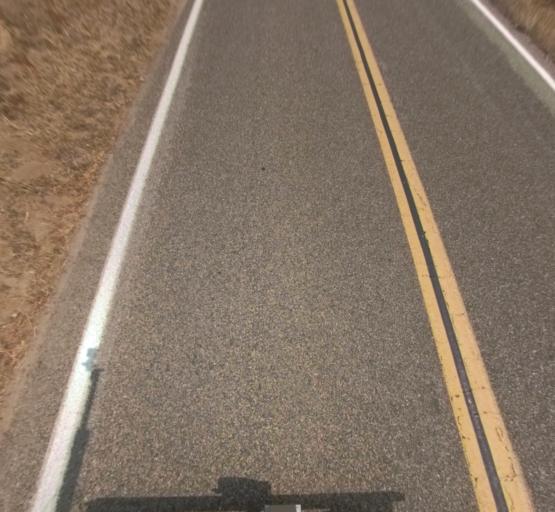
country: US
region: California
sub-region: Madera County
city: Yosemite Lakes
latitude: 37.1878
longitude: -119.9106
